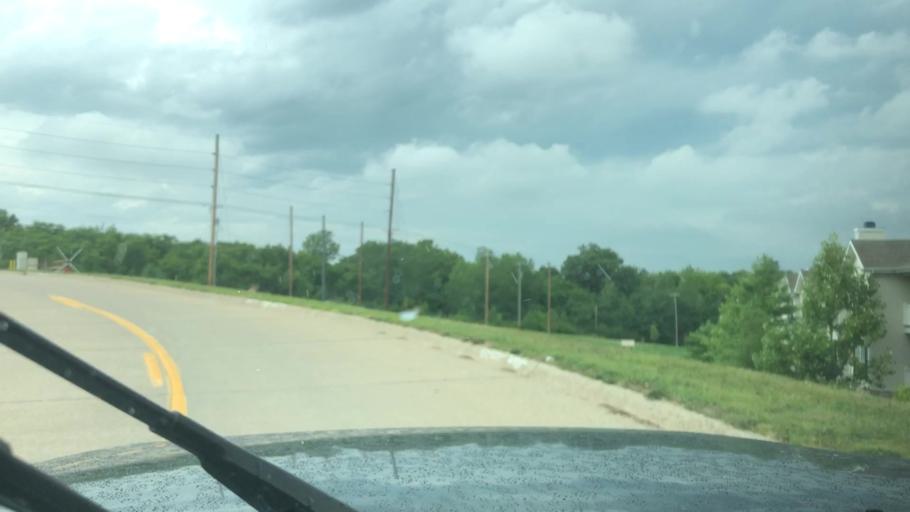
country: US
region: Missouri
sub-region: Saint Charles County
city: Saint Peters
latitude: 38.7990
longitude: -90.5792
